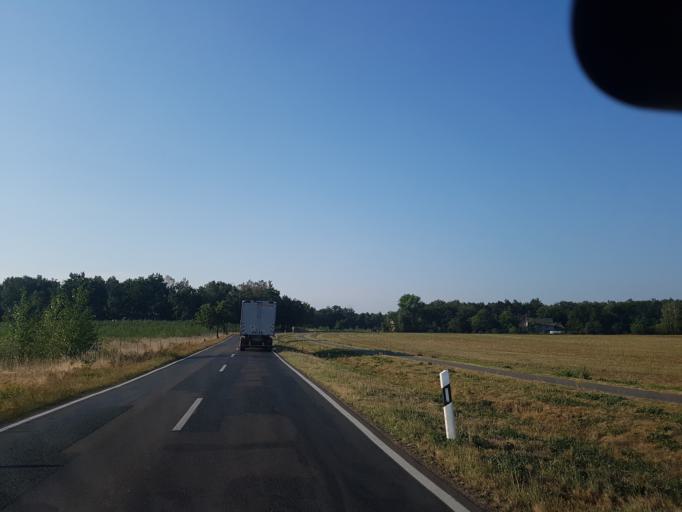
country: DE
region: Brandenburg
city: Hohenleipisch
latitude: 51.4773
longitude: 13.5492
